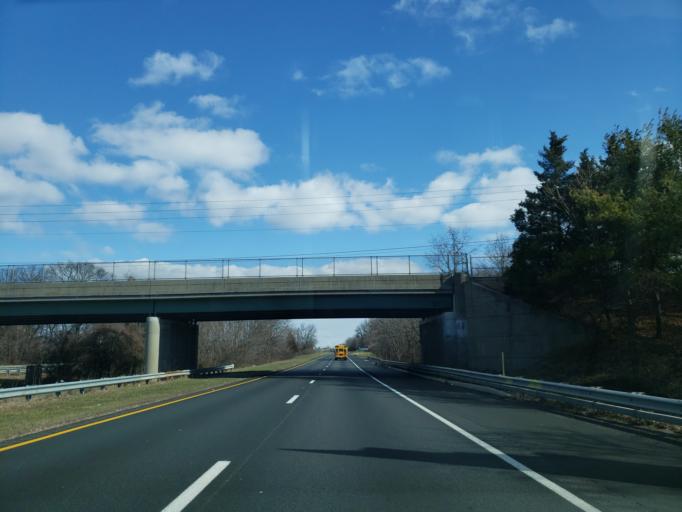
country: US
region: New Jersey
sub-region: Gloucester County
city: Beckett
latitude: 39.7656
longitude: -75.3556
